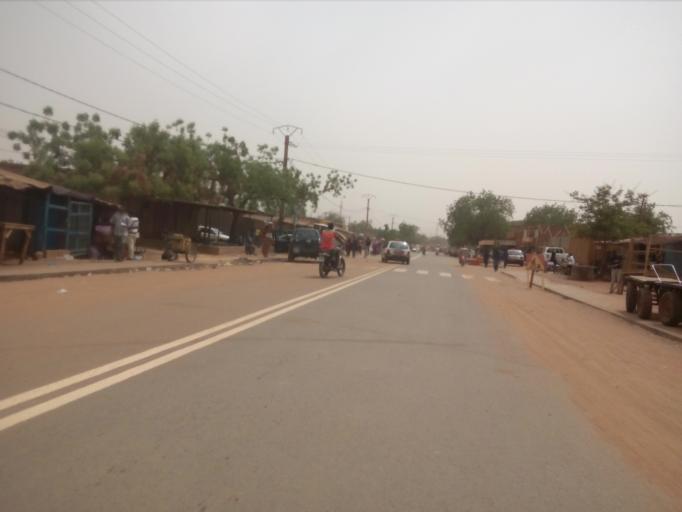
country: NE
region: Niamey
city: Niamey
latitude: 13.5284
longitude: 2.1219
